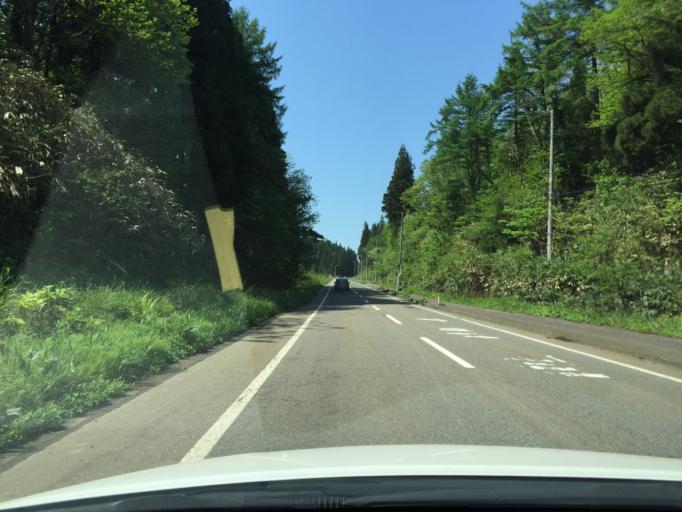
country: JP
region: Niigata
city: Kamo
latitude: 37.6073
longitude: 139.1032
